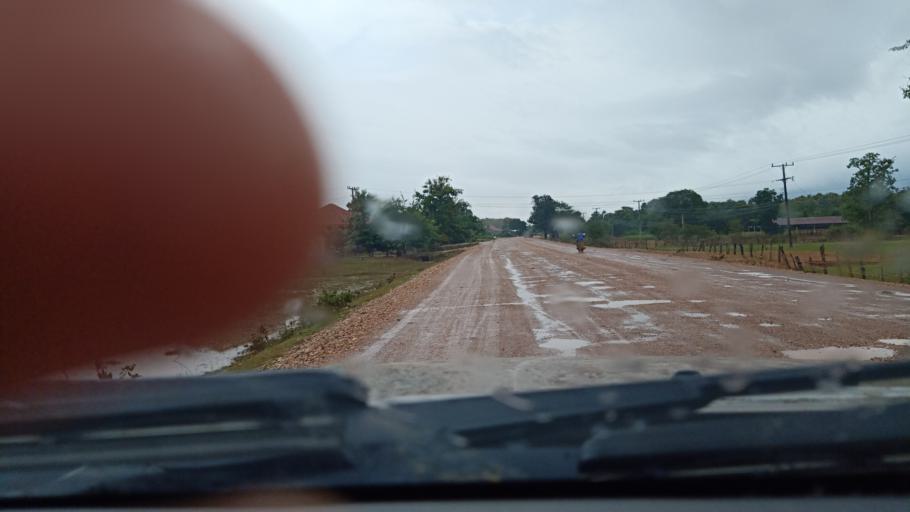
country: LA
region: Attapu
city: Attapu
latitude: 14.7130
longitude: 106.6636
